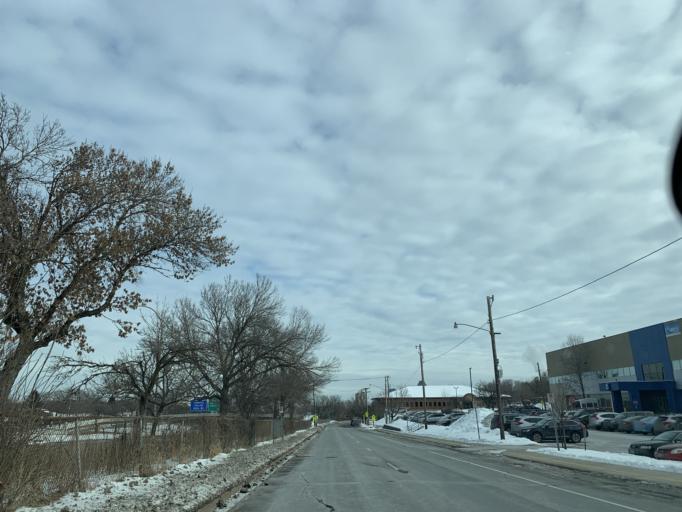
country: US
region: Minnesota
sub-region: Ramsey County
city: Saint Paul
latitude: 44.9514
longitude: -93.1229
